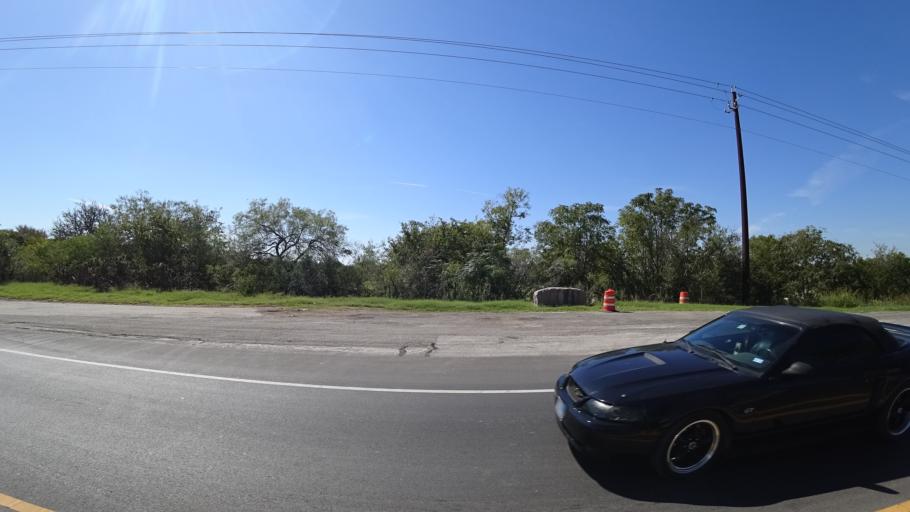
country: US
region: Texas
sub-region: Travis County
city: Hornsby Bend
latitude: 30.2552
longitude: -97.6082
